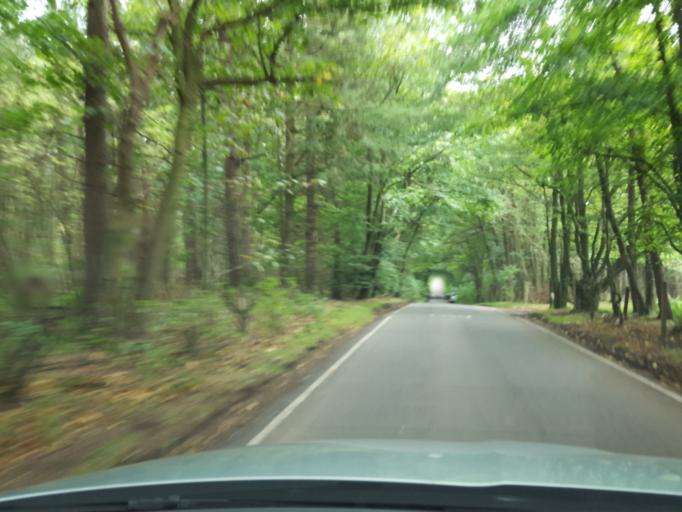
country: GB
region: Scotland
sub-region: West Lothian
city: Broxburn
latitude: 55.9153
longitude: -3.4586
